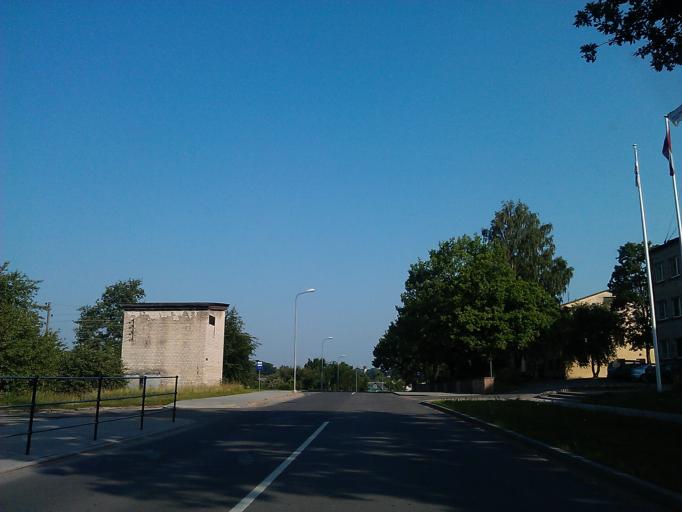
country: LV
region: Aizpute
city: Aizpute
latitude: 56.7067
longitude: 21.6230
